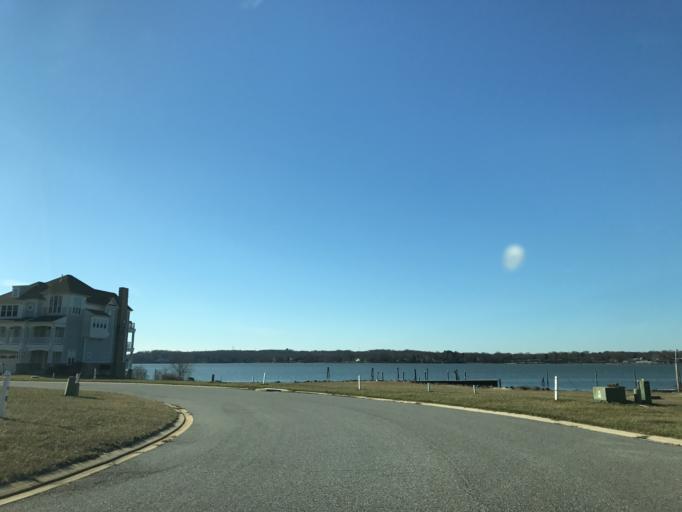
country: US
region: Maryland
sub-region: Harford County
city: Riverside
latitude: 39.4420
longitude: -76.2356
